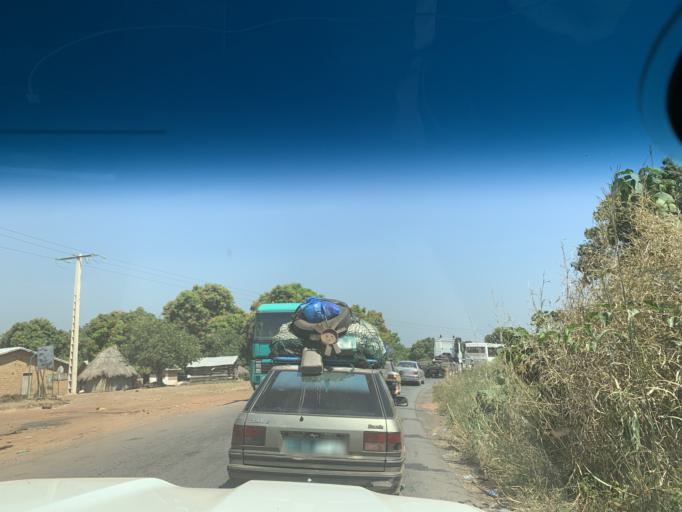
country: GN
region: Kindia
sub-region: Kindia
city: Kindia
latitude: 10.1800
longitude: -12.4938
